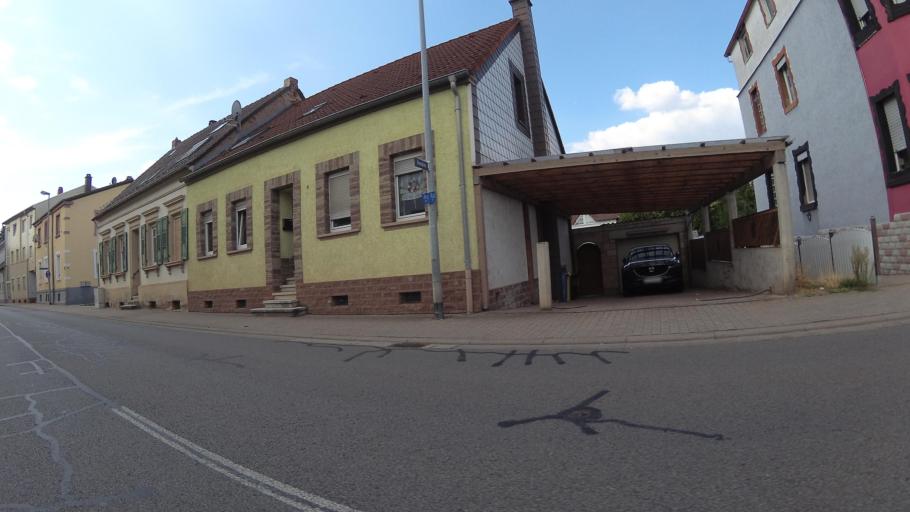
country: DE
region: Rheinland-Pfalz
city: Zweibrucken
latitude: 49.2367
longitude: 7.3618
